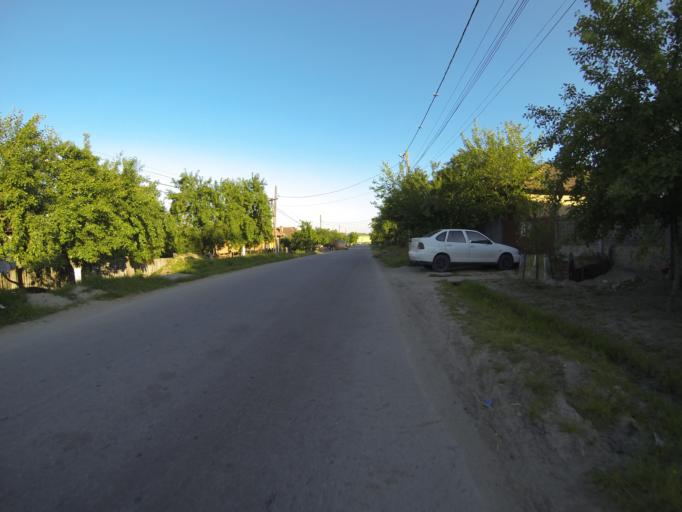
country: RO
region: Dolj
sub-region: Comuna Tuglui
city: Tuglui
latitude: 44.2041
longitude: 23.7981
